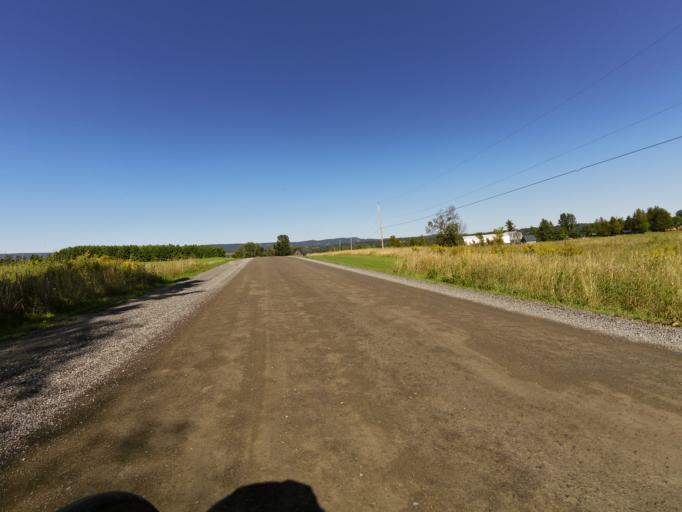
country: CA
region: Ontario
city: Bells Corners
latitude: 45.4378
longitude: -75.9561
